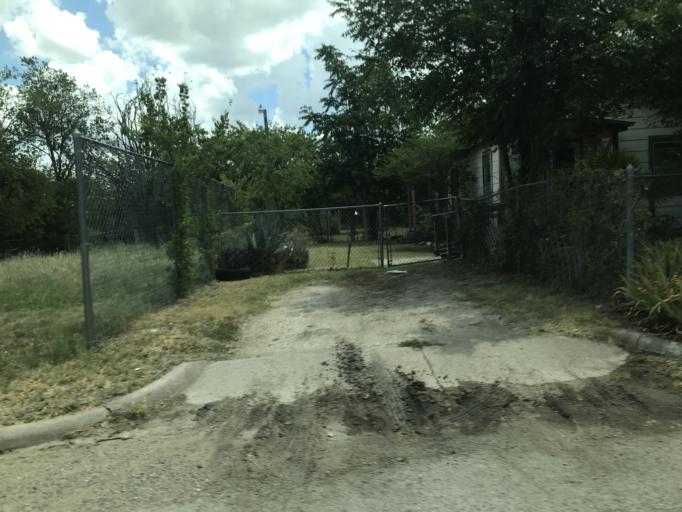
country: US
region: Texas
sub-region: Taylor County
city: Abilene
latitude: 32.4328
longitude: -99.7362
